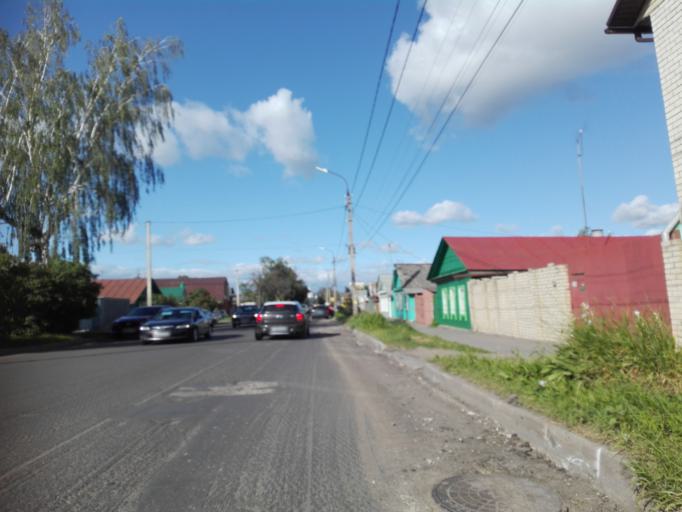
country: RU
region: Orjol
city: Orel
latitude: 52.9569
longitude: 36.0537
